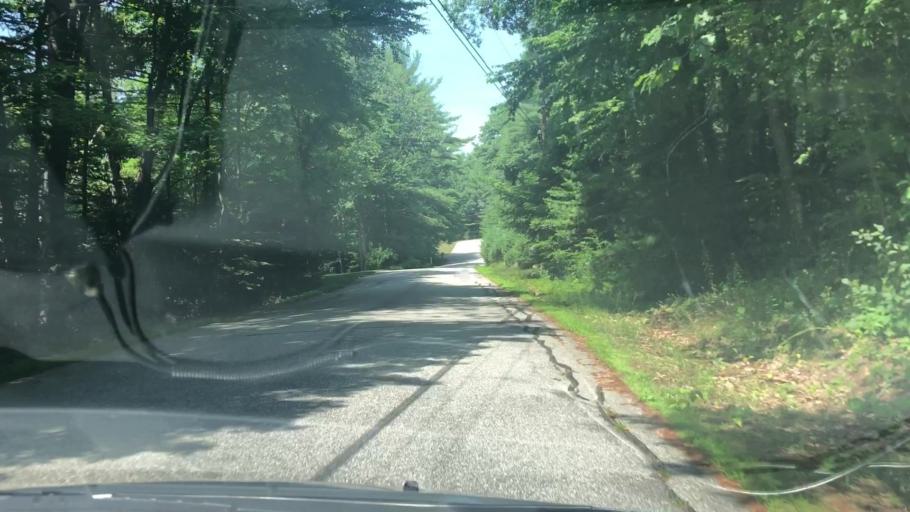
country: US
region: New Hampshire
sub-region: Hillsborough County
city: Milford
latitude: 42.8724
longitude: -71.6276
